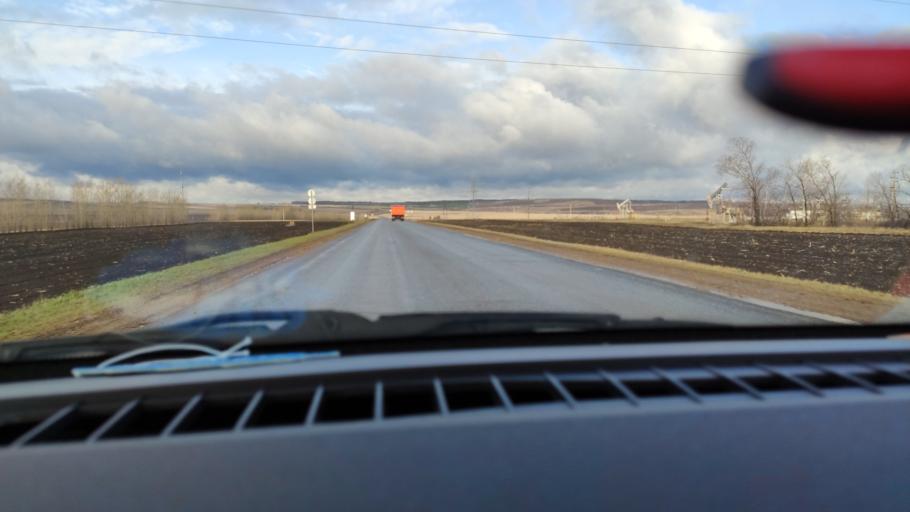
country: RU
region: Tatarstan
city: Russkiy Aktash
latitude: 55.0417
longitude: 52.0737
